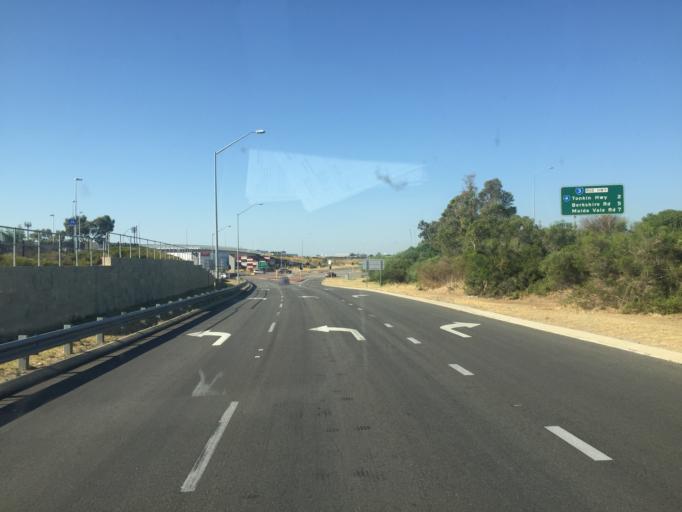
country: AU
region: Western Australia
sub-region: Canning
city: East Cannington
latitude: -32.0048
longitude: 115.9733
